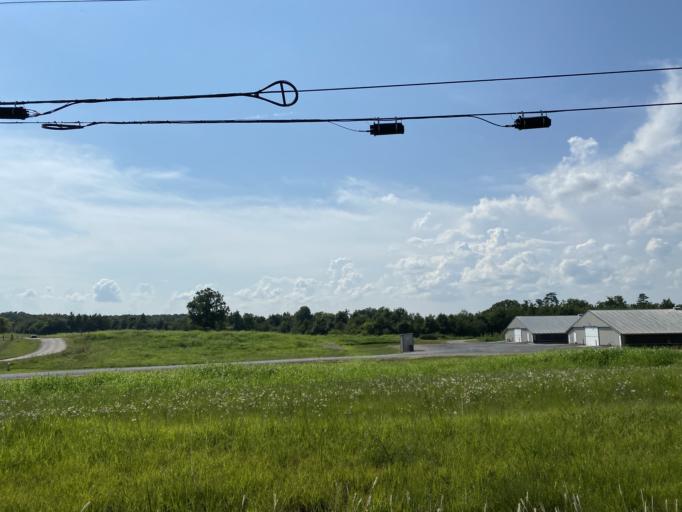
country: US
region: Alabama
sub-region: Lawrence County
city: Town Creek
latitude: 34.6321
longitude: -87.4080
